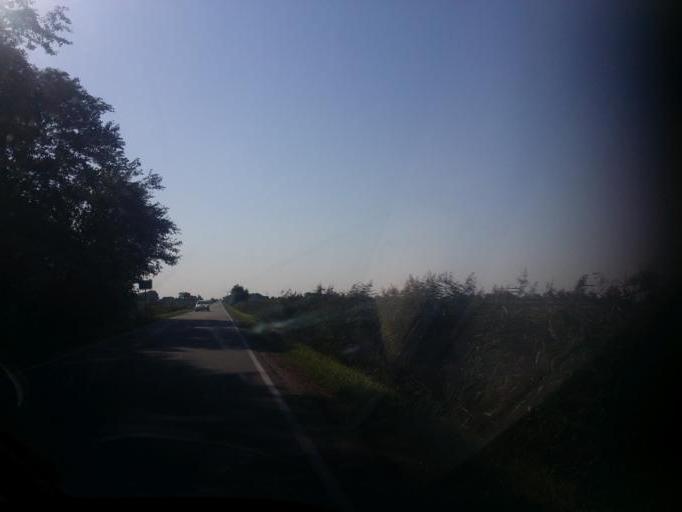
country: DE
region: Schleswig-Holstein
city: Emmelsbull-Horsbull
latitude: 54.8075
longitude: 8.7064
